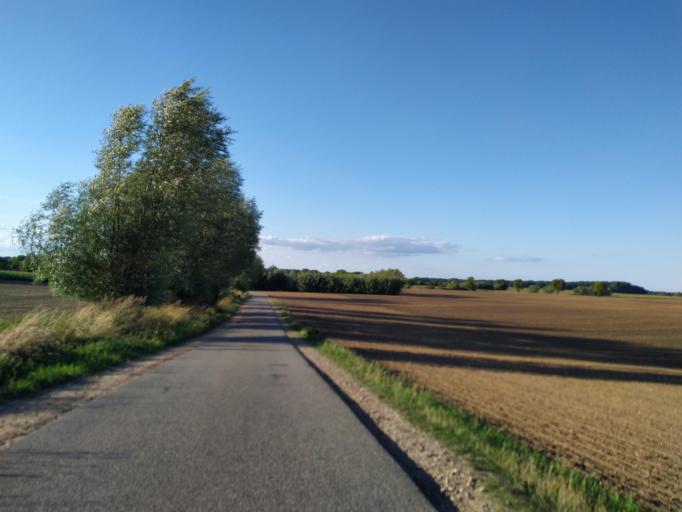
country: DE
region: Mecklenburg-Vorpommern
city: Kalkhorst
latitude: 53.9551
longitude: 11.0103
